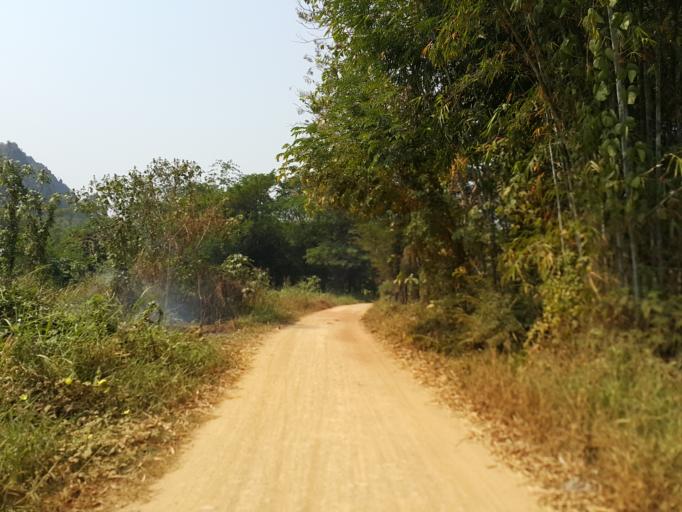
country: TH
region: Sukhothai
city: Thung Saliam
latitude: 17.3224
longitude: 99.5131
